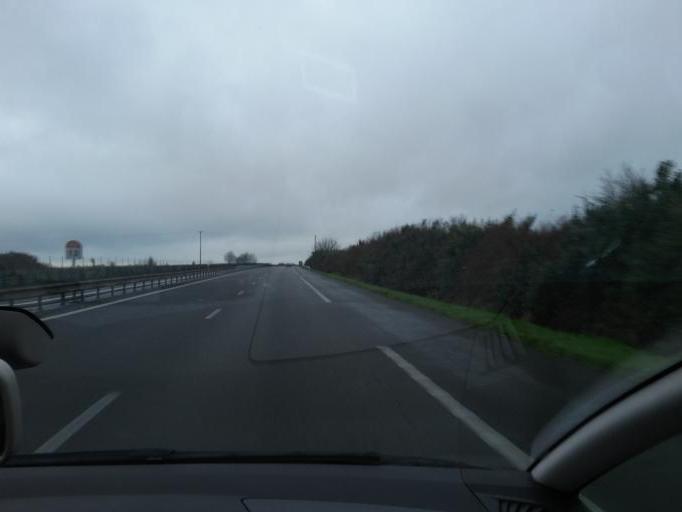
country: FR
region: Nord-Pas-de-Calais
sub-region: Departement du Pas-de-Calais
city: Hermies
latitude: 50.0779
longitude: 3.0225
